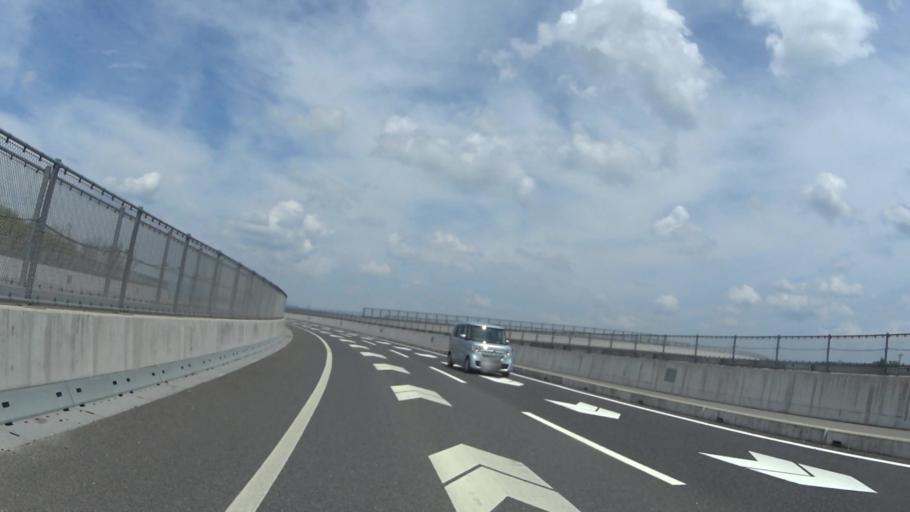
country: JP
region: Kyoto
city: Yawata
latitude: 34.8436
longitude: 135.7180
